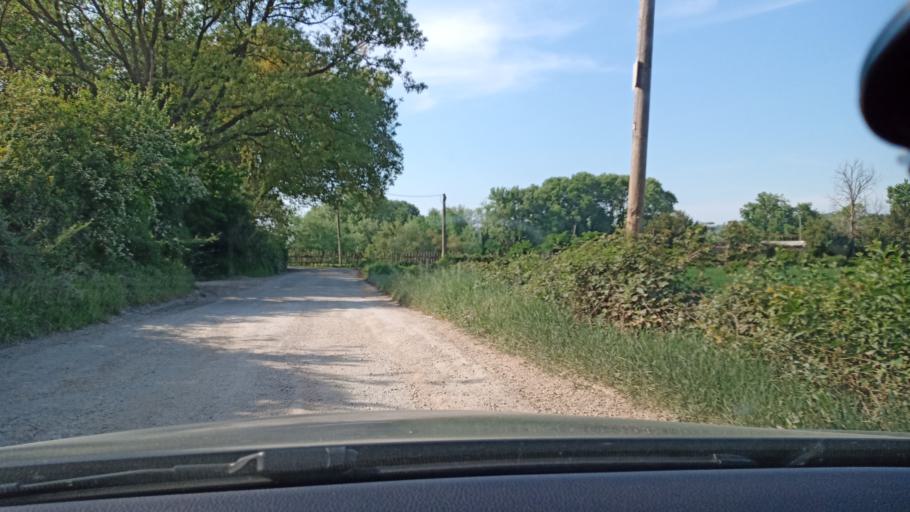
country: IT
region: Latium
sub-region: Citta metropolitana di Roma Capitale
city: Ponzano Romano
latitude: 42.2678
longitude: 12.5603
